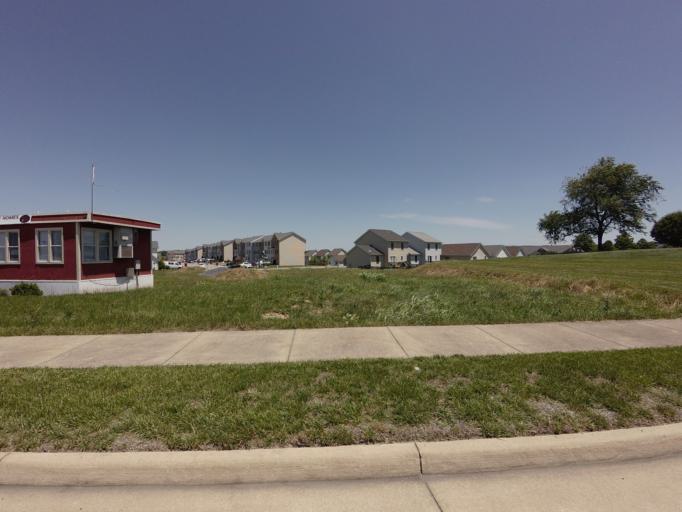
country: US
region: West Virginia
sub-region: Jefferson County
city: Ranson
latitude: 39.3211
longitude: -77.8462
